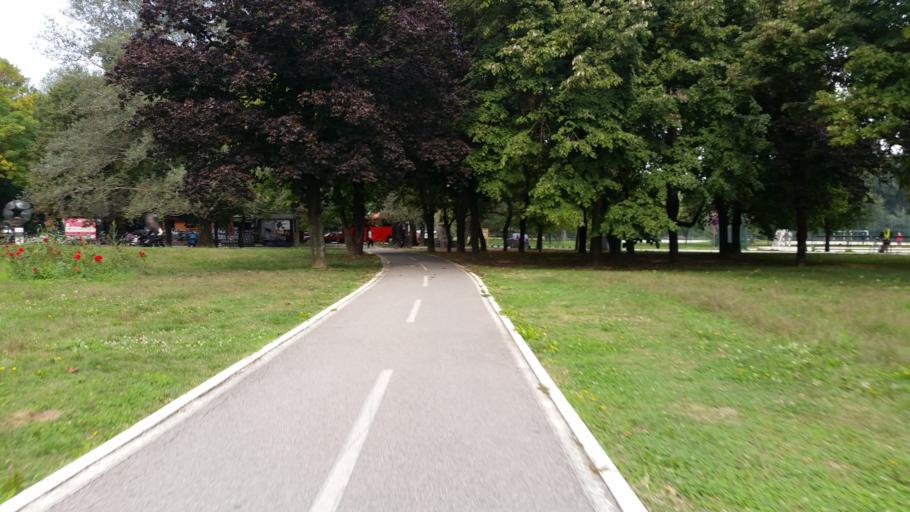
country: RS
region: Central Serbia
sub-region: Belgrade
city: Cukarica
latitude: 44.7898
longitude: 20.4140
